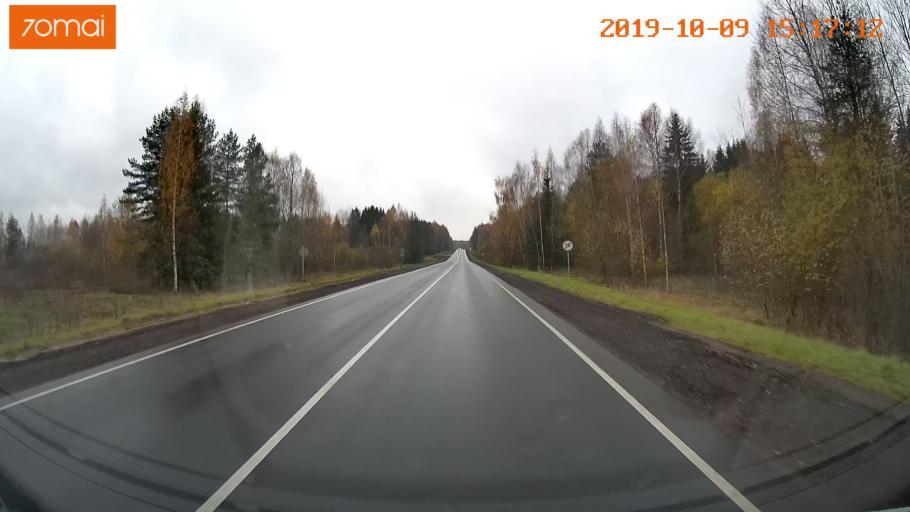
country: RU
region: Kostroma
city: Susanino
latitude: 58.1014
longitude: 41.5836
